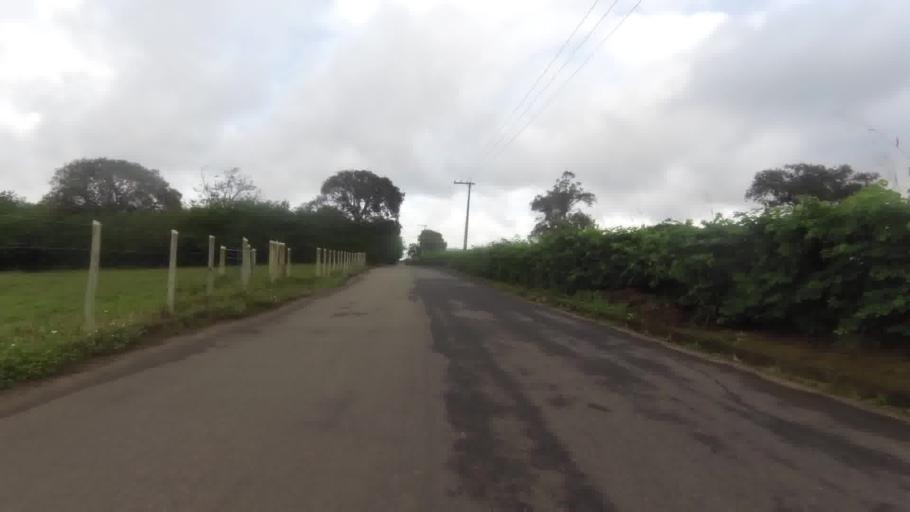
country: BR
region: Espirito Santo
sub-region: Piuma
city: Piuma
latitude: -20.7659
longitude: -40.6310
